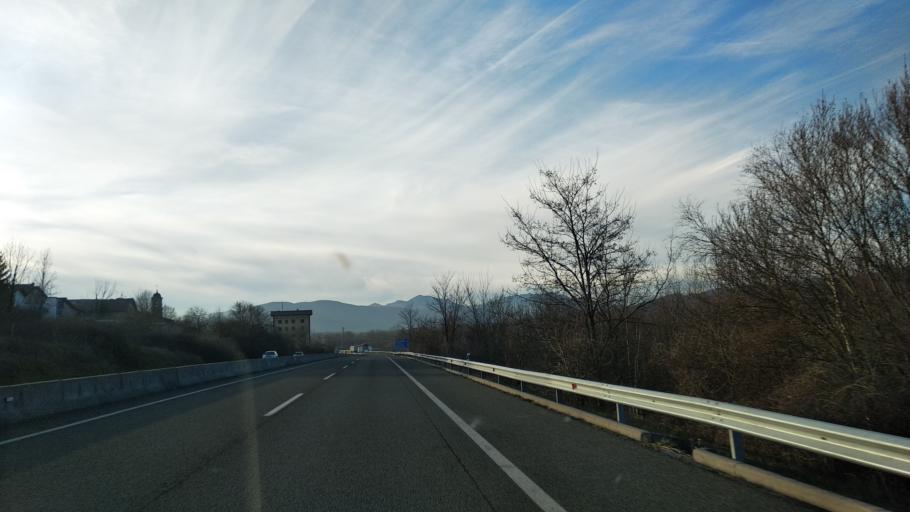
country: ES
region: Navarre
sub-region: Provincia de Navarra
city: Bakaiku
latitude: 42.8932
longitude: -2.0988
